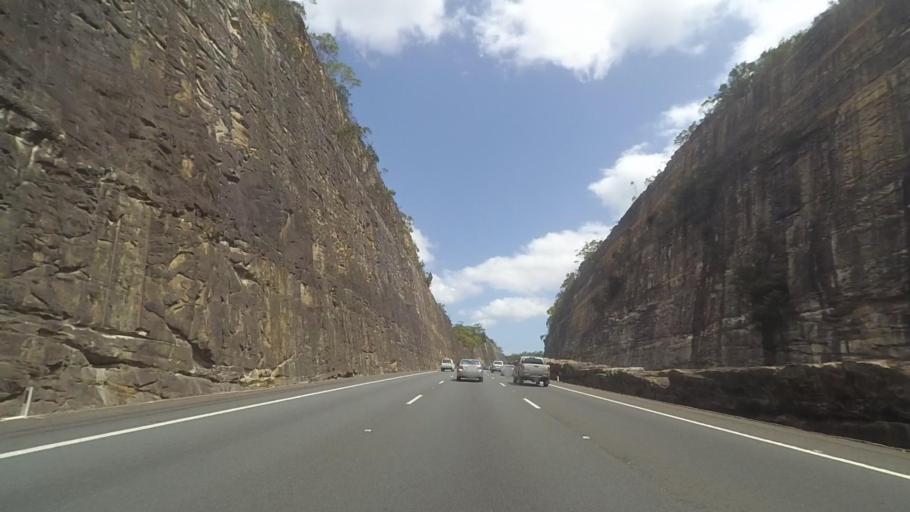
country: AU
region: New South Wales
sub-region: Hornsby Shire
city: Berowra
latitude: -33.5711
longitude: 151.1930
